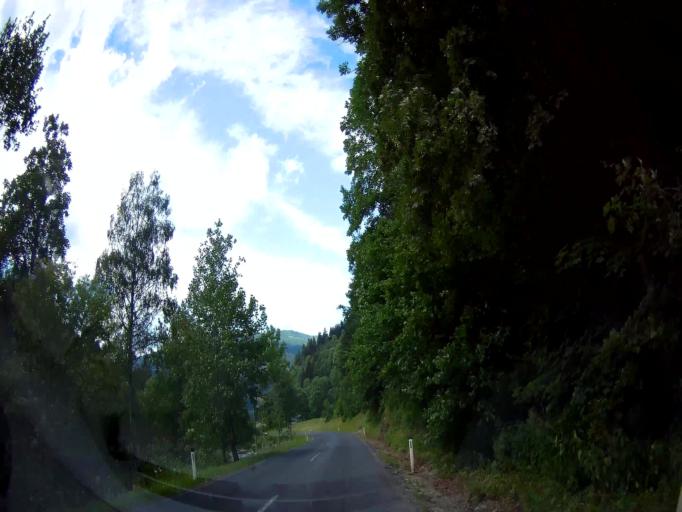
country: AT
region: Styria
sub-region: Politischer Bezirk Murau
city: Stadl an der Mur
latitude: 47.0691
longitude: 13.9853
